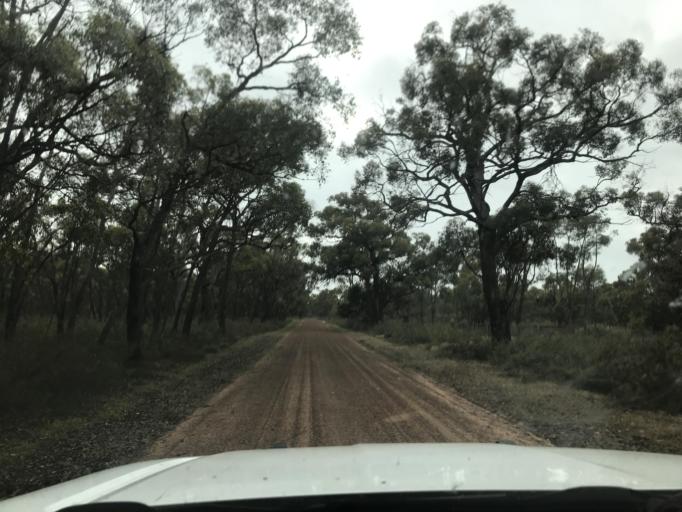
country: AU
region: South Australia
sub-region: Wattle Range
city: Penola
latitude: -37.1177
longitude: 141.1252
